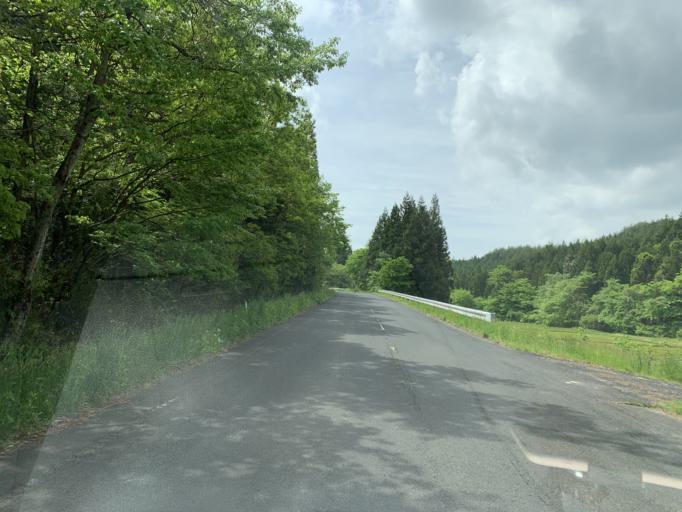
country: JP
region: Iwate
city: Ichinoseki
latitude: 38.8787
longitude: 140.9753
